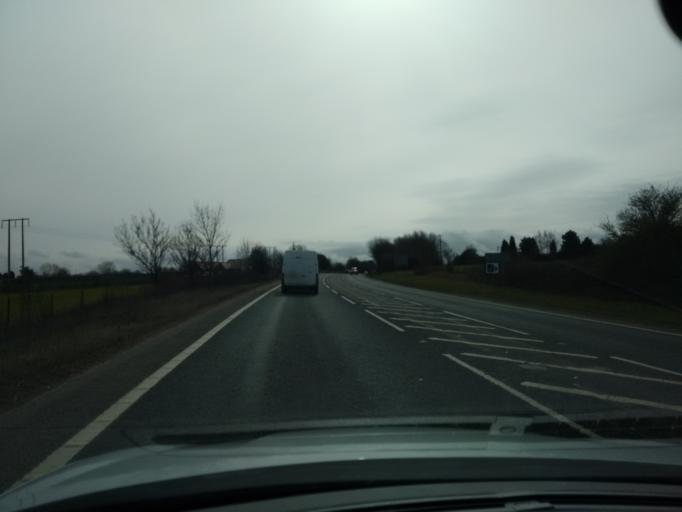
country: GB
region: England
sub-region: Worcestershire
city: Evesham
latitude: 52.1021
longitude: -1.9245
